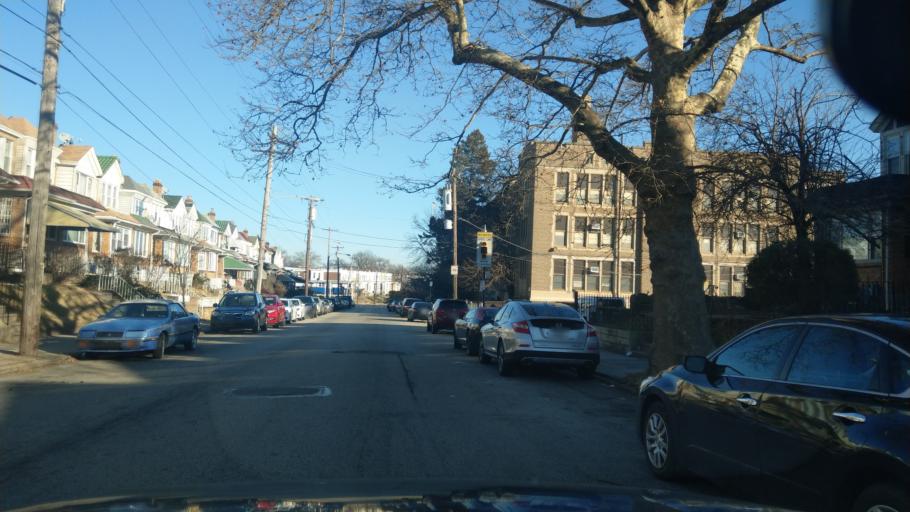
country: US
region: Pennsylvania
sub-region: Montgomery County
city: Wyncote
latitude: 40.0436
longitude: -75.1519
